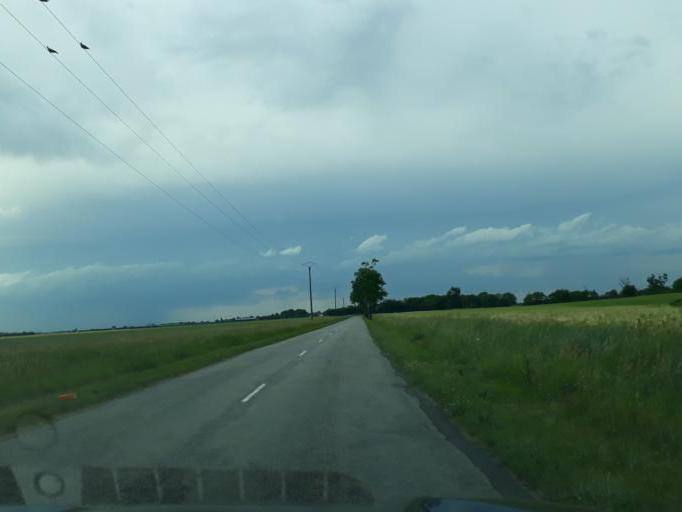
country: FR
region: Centre
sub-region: Departement du Loiret
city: Vienne-en-Val
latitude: 47.8225
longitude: 2.1570
